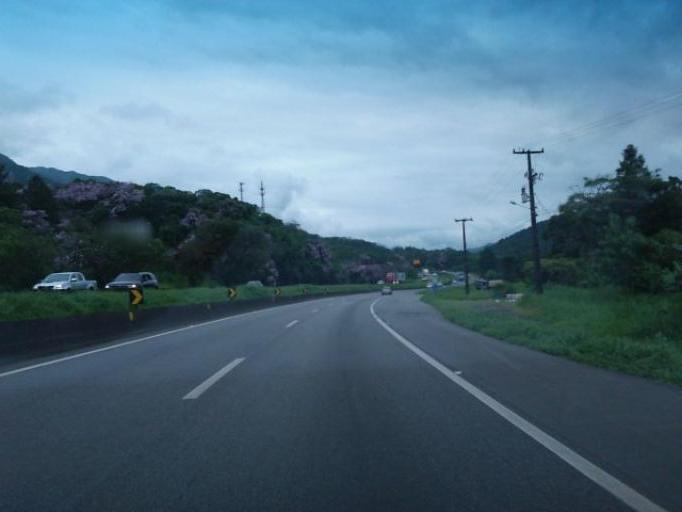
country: BR
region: Parana
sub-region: Guaratuba
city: Guaratuba
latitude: -25.9653
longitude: -48.8970
